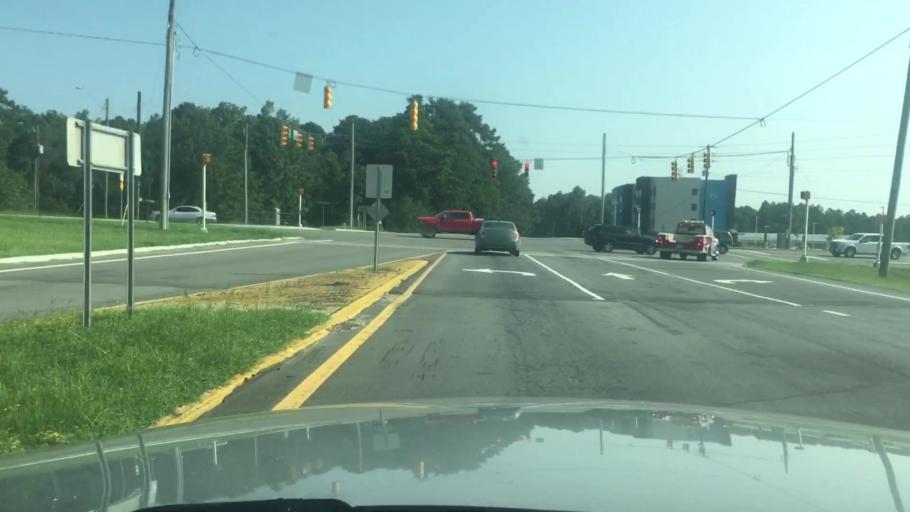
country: US
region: North Carolina
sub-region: Cumberland County
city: Vander
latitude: 35.0065
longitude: -78.8188
